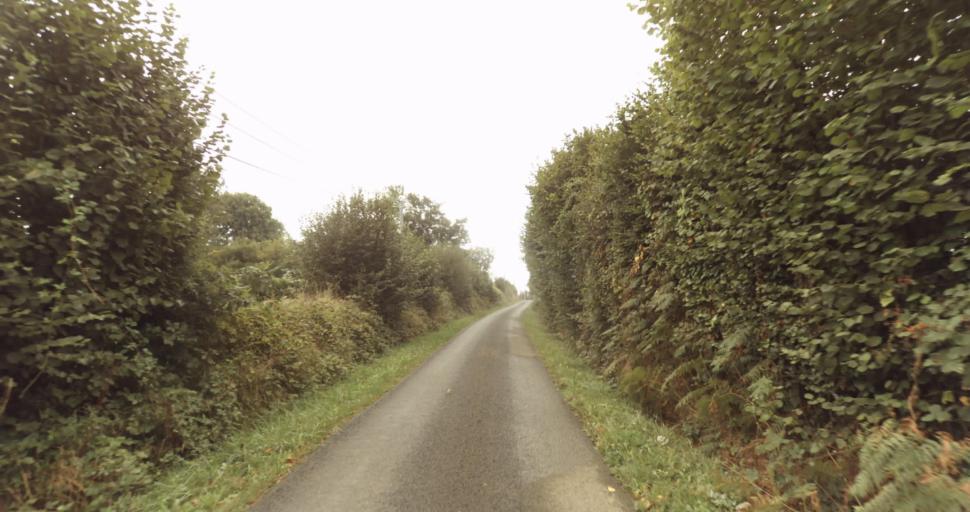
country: FR
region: Lower Normandy
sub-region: Departement de l'Orne
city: Sainte-Gauburge-Sainte-Colombe
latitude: 48.7343
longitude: 0.4354
